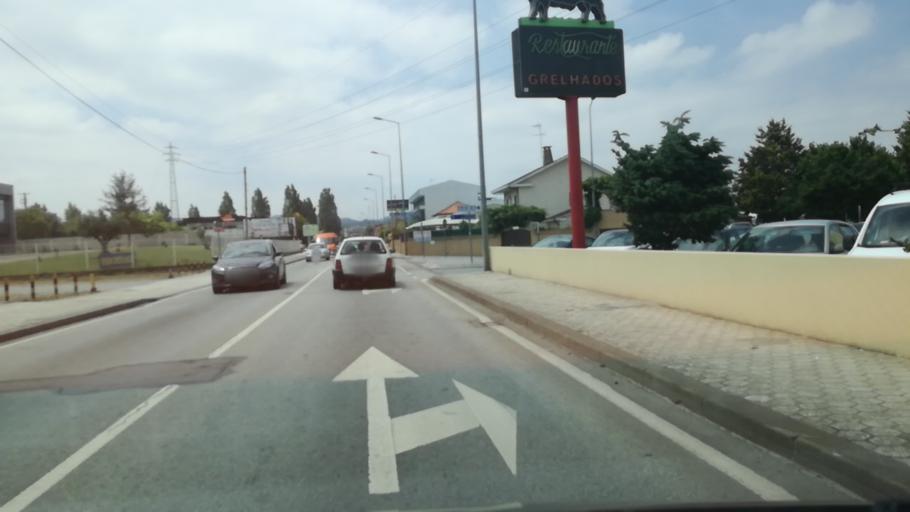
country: PT
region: Porto
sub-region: Trofa
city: Bougado
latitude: 41.3282
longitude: -8.5667
